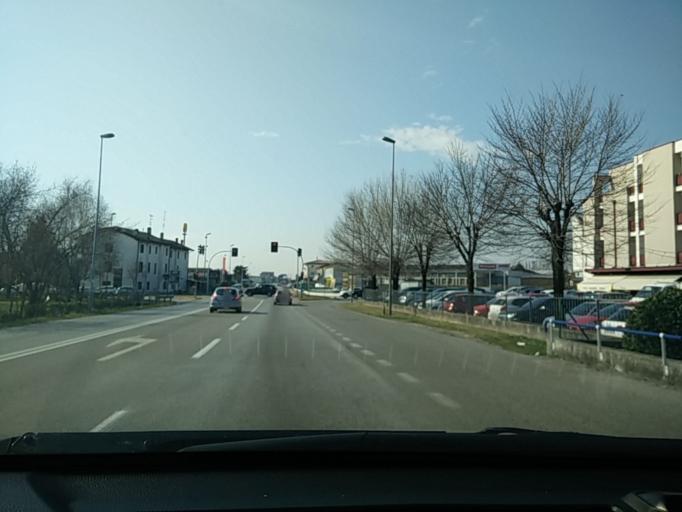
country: IT
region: Veneto
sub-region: Provincia di Treviso
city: San Vendemiano-Fossamerlo
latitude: 45.8924
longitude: 12.3273
